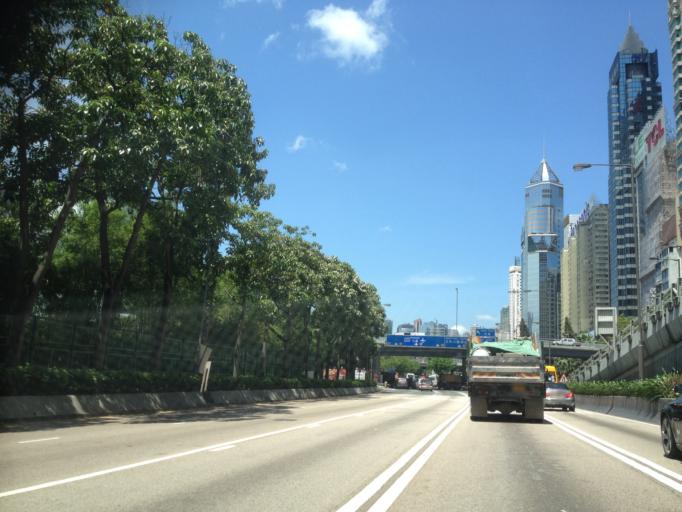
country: HK
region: Wanchai
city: Wan Chai
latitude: 22.2801
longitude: 114.1780
